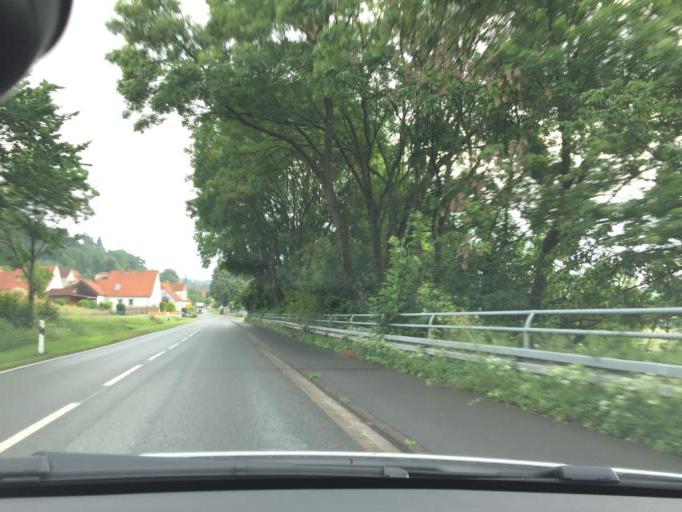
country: DE
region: Lower Saxony
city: Hameln
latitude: 52.0217
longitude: 9.3417
